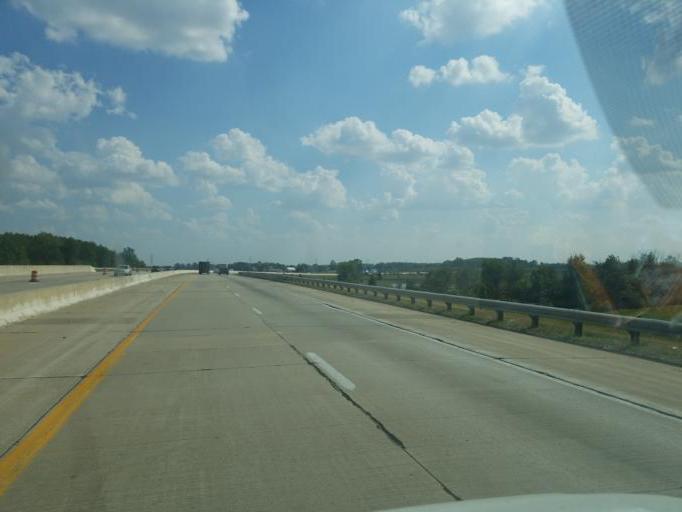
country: US
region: Indiana
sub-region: Allen County
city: New Haven
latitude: 41.1290
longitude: -85.0002
